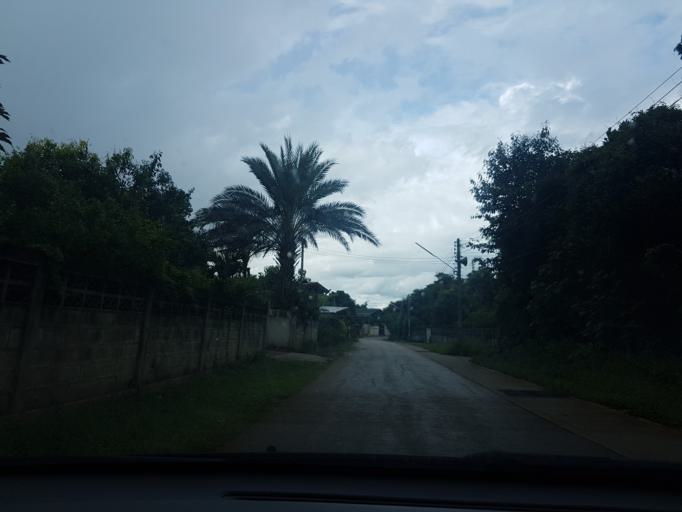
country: TH
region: Lampang
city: Ko Kha
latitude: 18.2367
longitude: 99.4274
